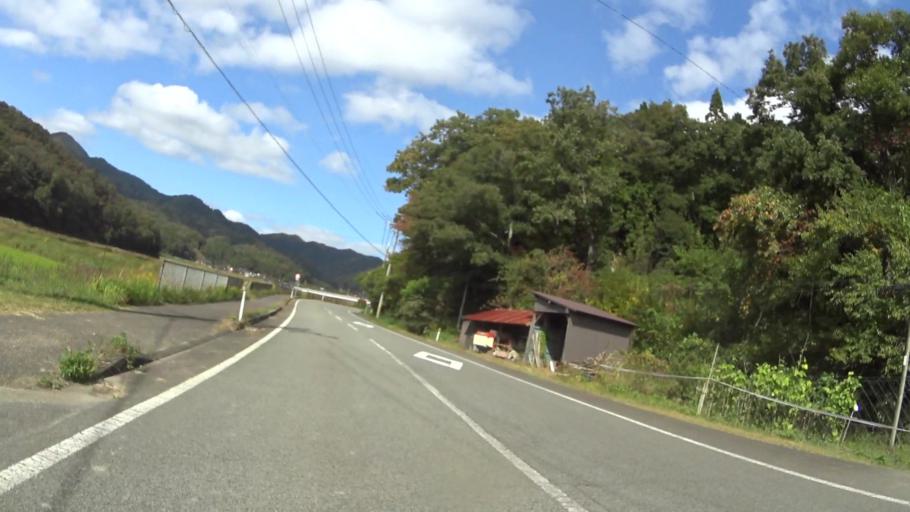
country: JP
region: Hyogo
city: Toyooka
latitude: 35.5006
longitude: 134.9925
